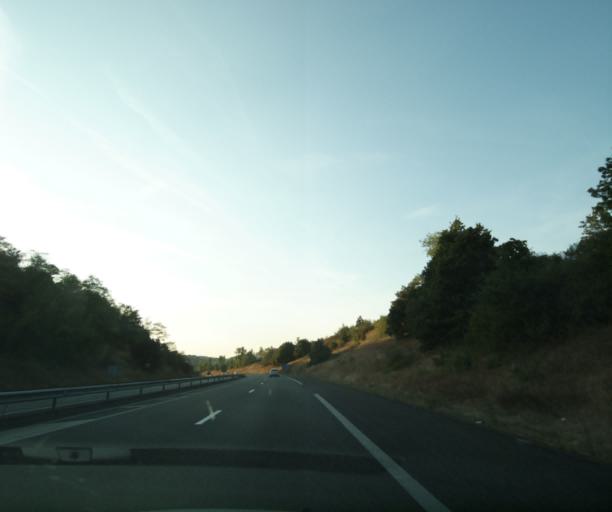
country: FR
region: Aquitaine
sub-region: Departement du Lot-et-Garonne
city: Boe
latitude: 44.1440
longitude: 0.6328
